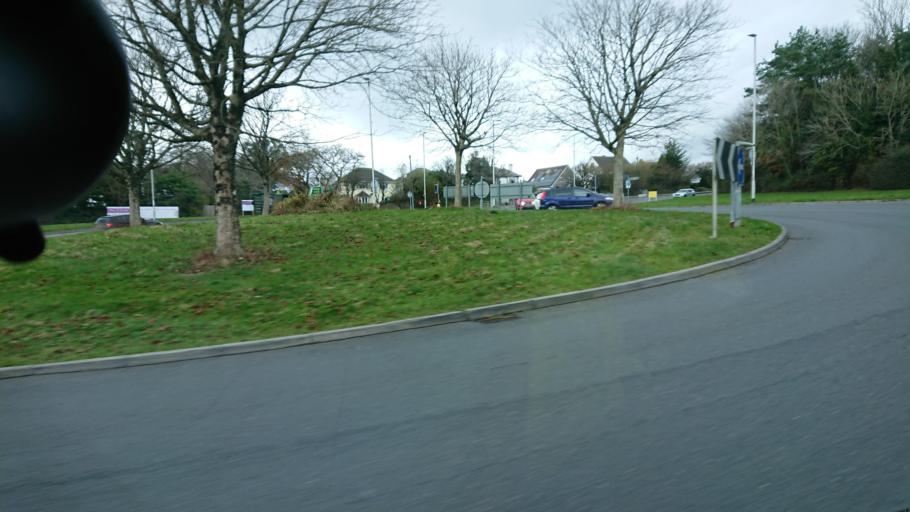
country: GB
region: England
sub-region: Devon
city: Yelverton
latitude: 50.4334
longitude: -4.1103
